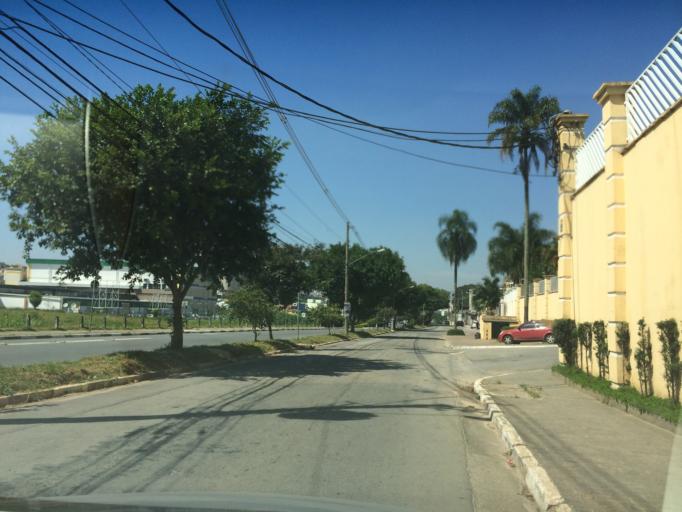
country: BR
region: Sao Paulo
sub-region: Guarulhos
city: Guarulhos
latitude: -23.4272
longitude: -46.5392
